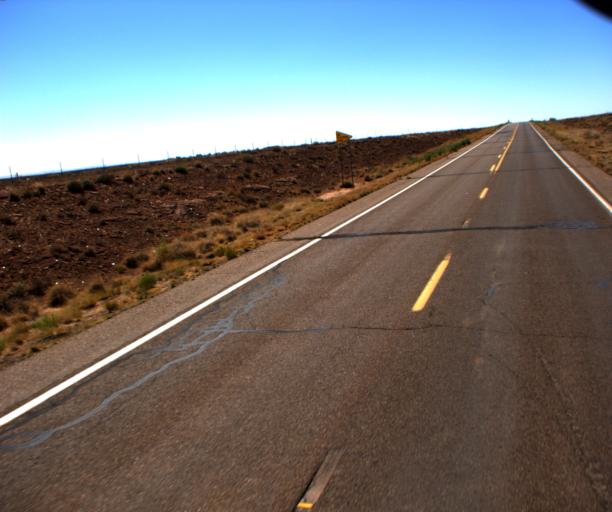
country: US
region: Arizona
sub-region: Coconino County
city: LeChee
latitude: 35.2938
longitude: -110.9900
